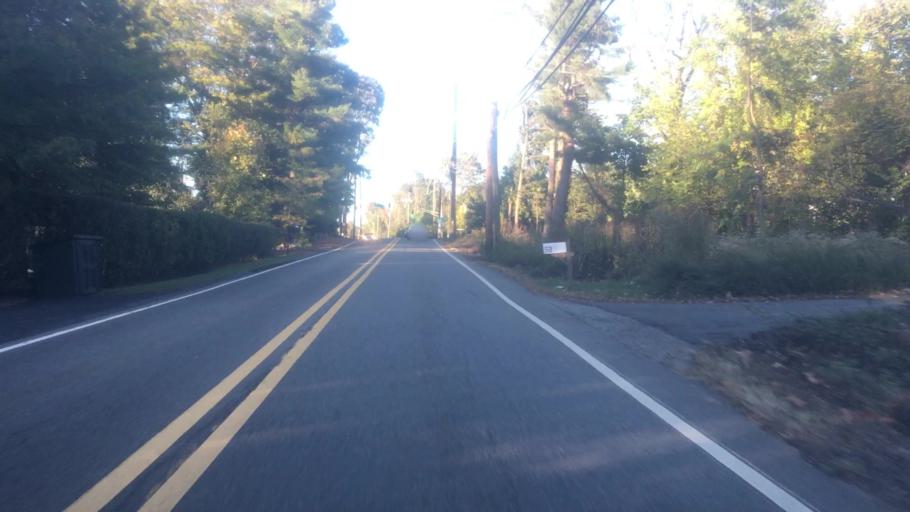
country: US
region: New Jersey
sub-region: Bergen County
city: Franklin Lakes
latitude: 40.9934
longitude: -74.1988
